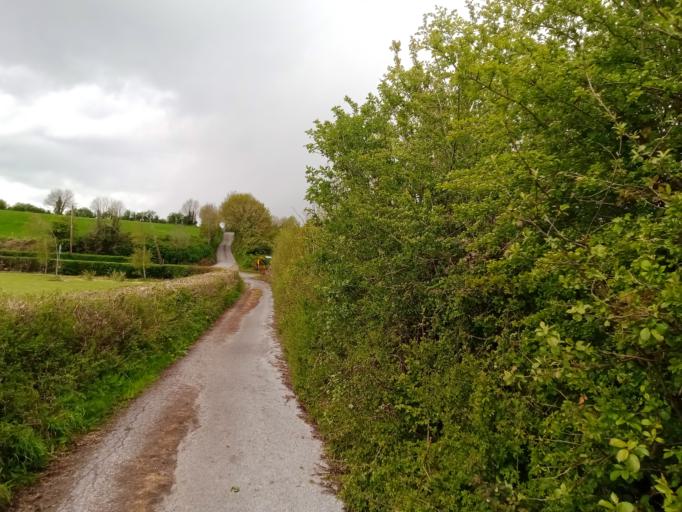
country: IE
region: Leinster
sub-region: Kilkenny
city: Kilkenny
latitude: 52.6941
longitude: -7.2699
